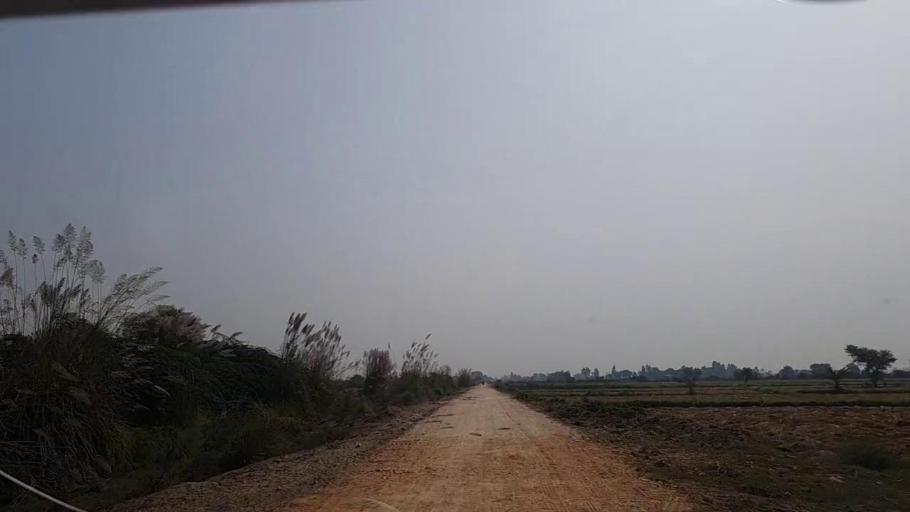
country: PK
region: Sindh
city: Garhi Yasin
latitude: 27.9276
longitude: 68.5626
